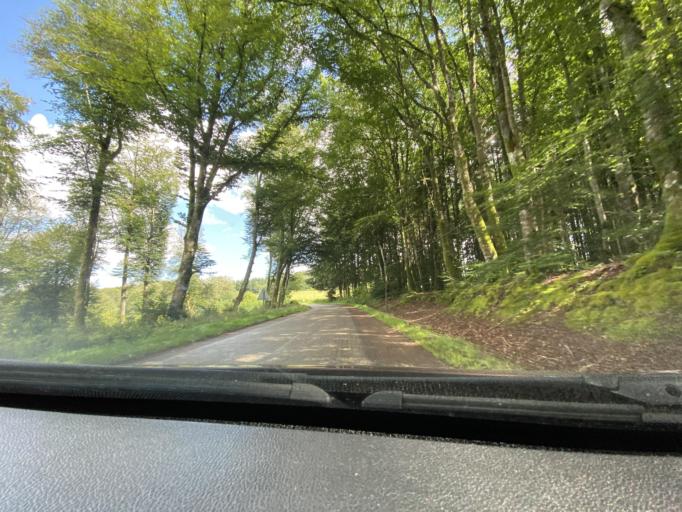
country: FR
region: Bourgogne
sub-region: Departement de la Cote-d'Or
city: Saulieu
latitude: 47.2567
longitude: 4.1018
